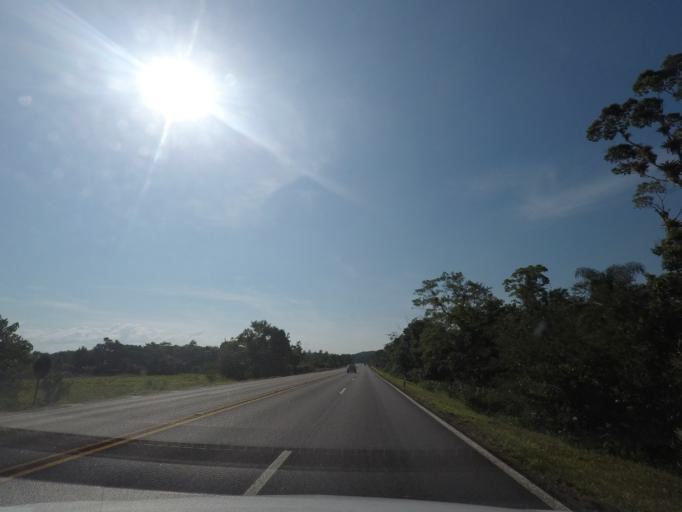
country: BR
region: Parana
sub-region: Paranagua
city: Paranagua
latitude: -25.5800
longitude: -48.6124
